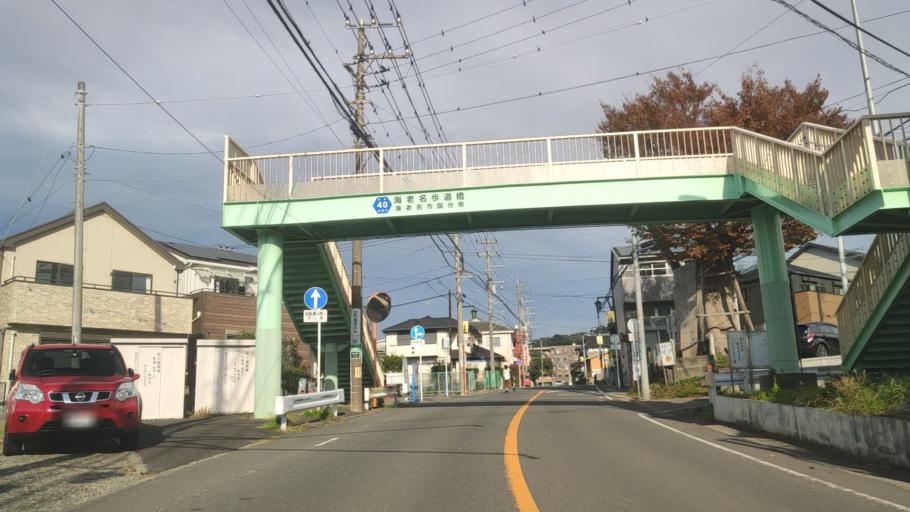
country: JP
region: Kanagawa
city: Zama
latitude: 35.4522
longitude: 139.3976
